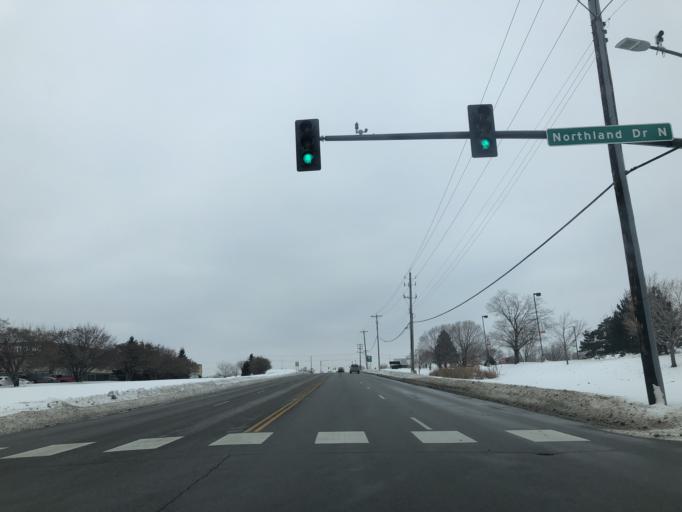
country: US
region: Minnesota
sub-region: Hennepin County
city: Osseo
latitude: 45.0946
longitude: -93.3959
